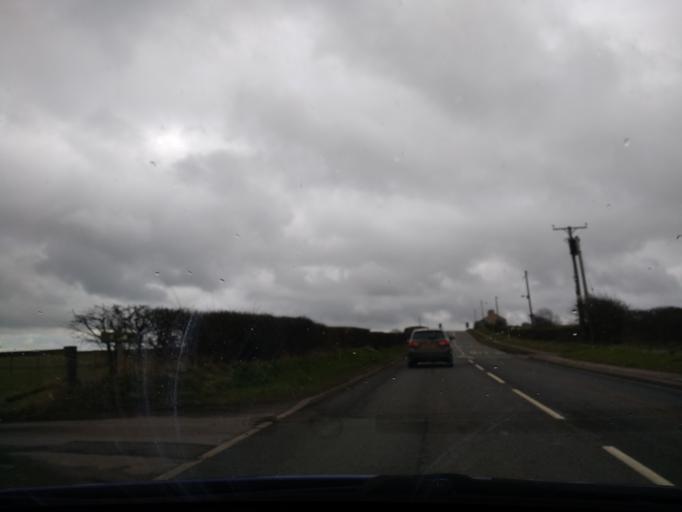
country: GB
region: England
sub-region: Cumbria
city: Dearham
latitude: 54.7014
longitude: -3.4454
